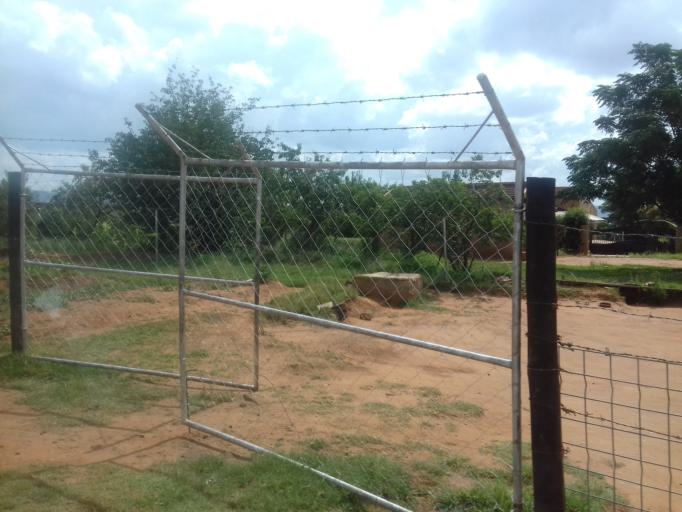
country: LS
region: Maseru
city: Maseru
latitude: -29.4209
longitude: 27.5652
